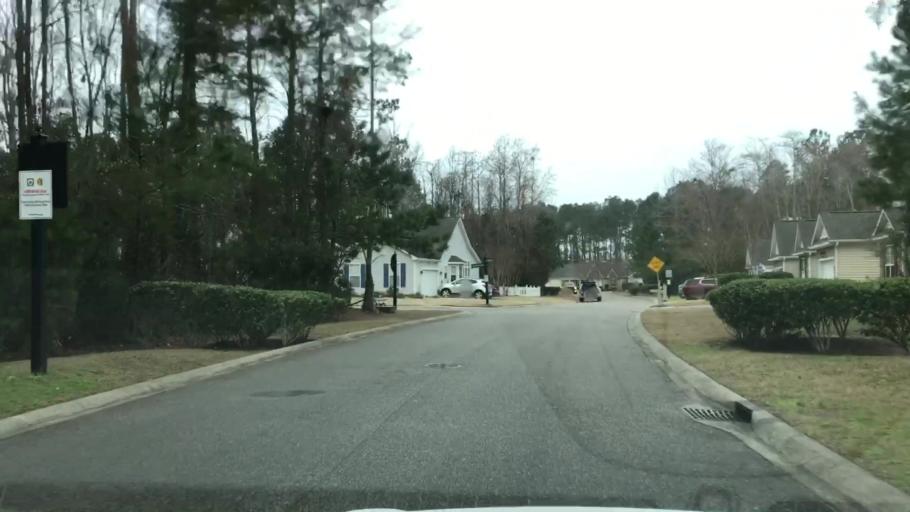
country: US
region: South Carolina
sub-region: Horry County
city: Red Hill
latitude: 33.7776
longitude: -79.0090
